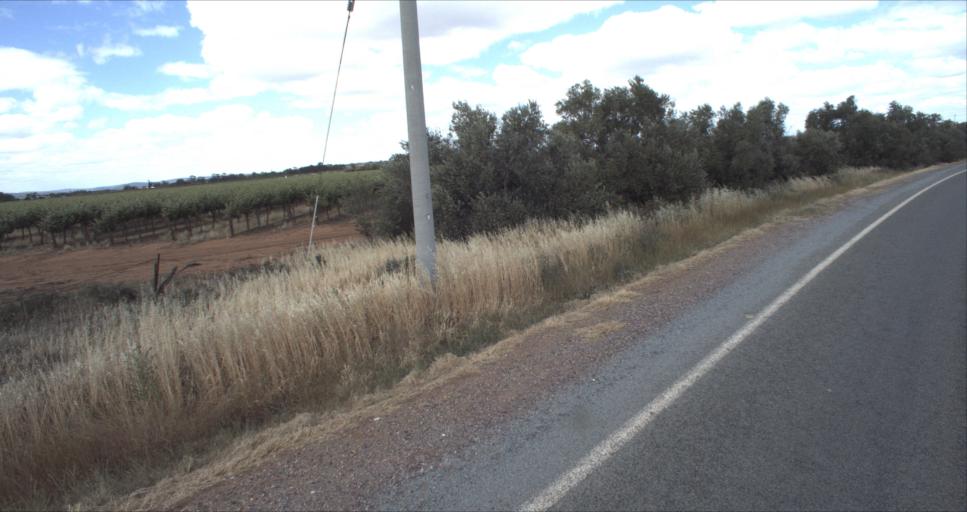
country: AU
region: New South Wales
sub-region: Leeton
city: Leeton
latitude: -34.5807
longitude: 146.4002
